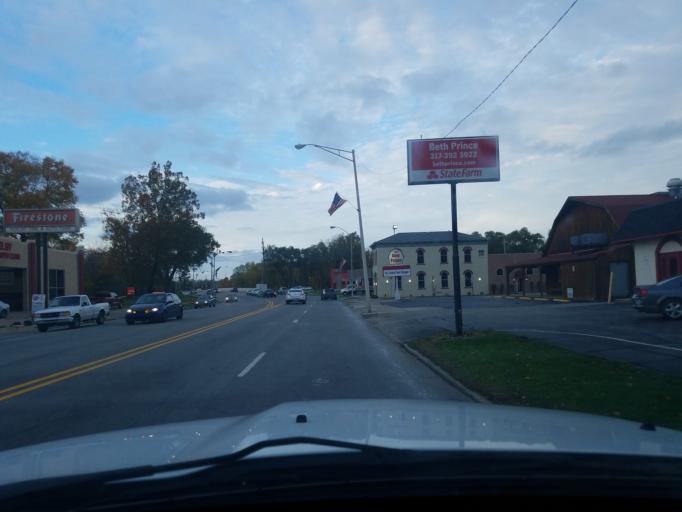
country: US
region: Indiana
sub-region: Shelby County
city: Shelbyville
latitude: 39.5269
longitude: -85.7769
